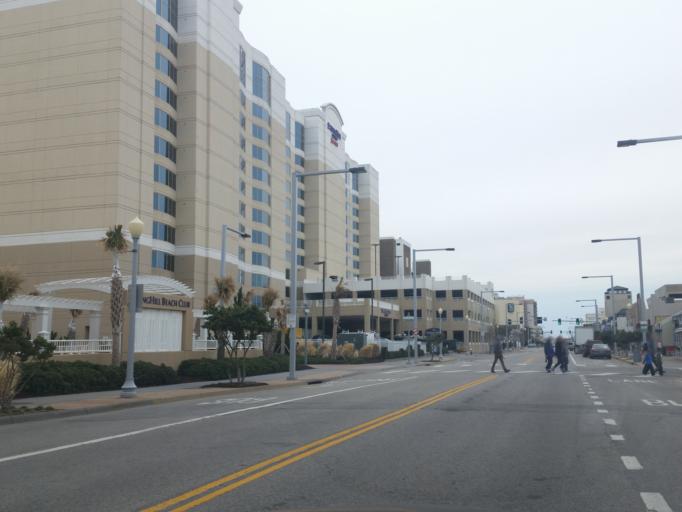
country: US
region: Virginia
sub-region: City of Virginia Beach
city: Virginia Beach
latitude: 36.8390
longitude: -75.9726
